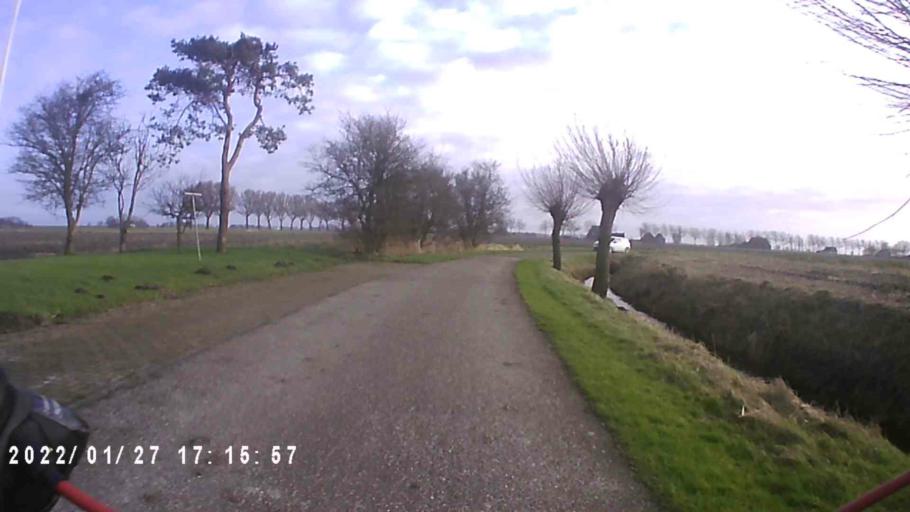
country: NL
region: Friesland
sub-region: Gemeente Dongeradeel
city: Anjum
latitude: 53.3922
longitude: 6.0979
